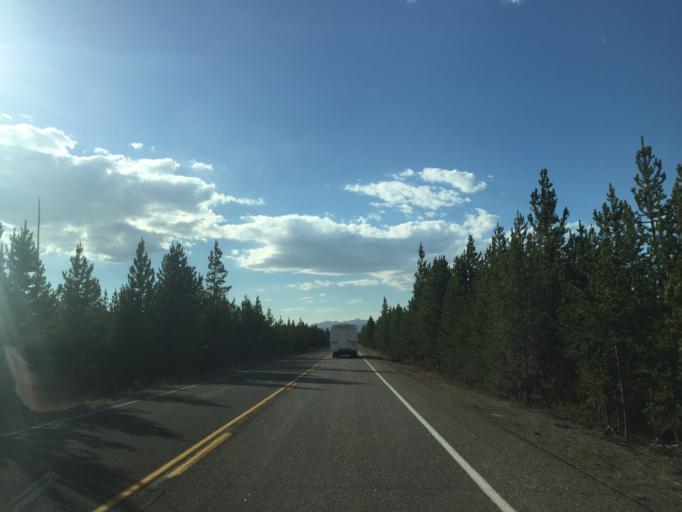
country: US
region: Montana
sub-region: Gallatin County
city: West Yellowstone
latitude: 44.6500
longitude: -111.0198
